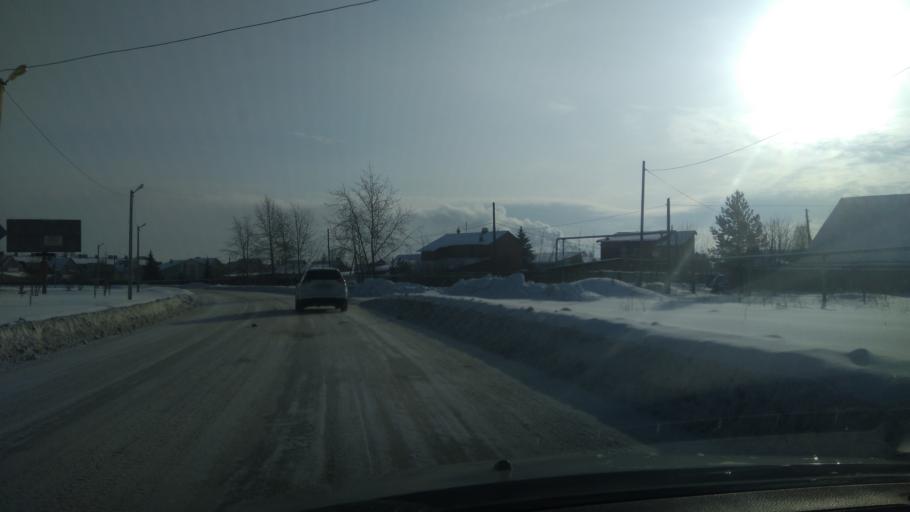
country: RU
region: Sverdlovsk
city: Sukhoy Log
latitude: 56.8919
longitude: 62.0350
